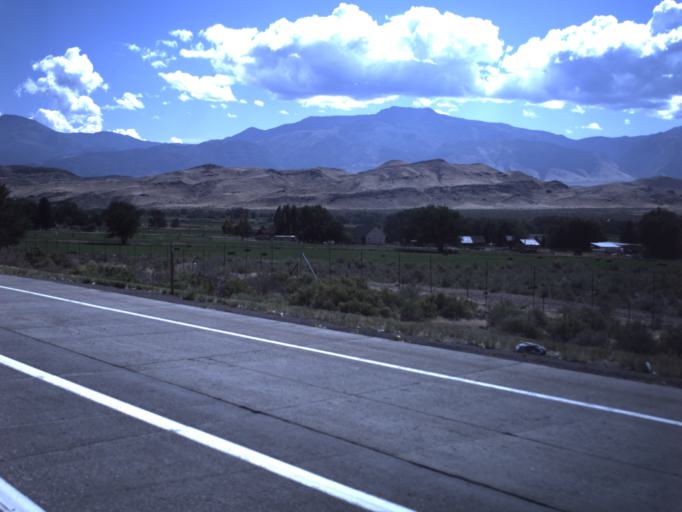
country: US
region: Utah
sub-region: Sevier County
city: Monroe
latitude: 38.6010
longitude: -112.2489
